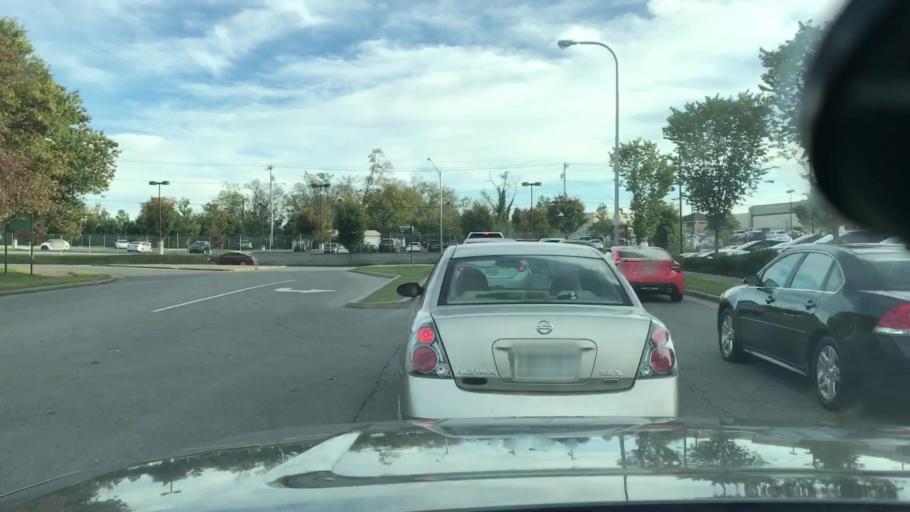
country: US
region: Tennessee
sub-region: Davidson County
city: Nashville
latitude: 36.1890
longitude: -86.7971
